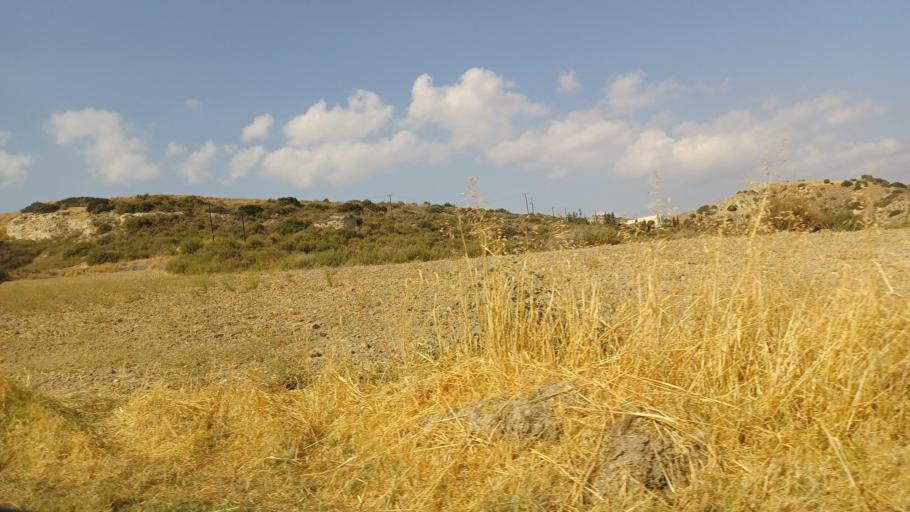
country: CY
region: Pafos
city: Polis
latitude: 34.9961
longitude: 32.4356
